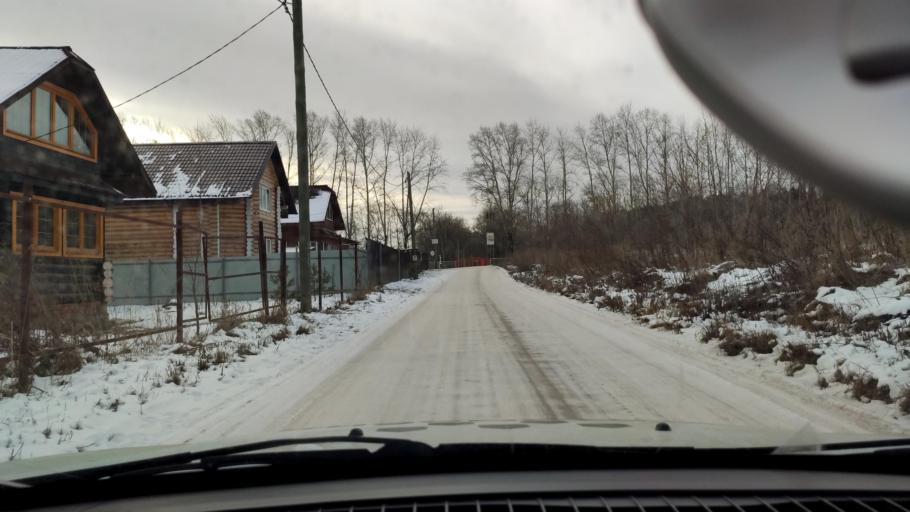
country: RU
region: Perm
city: Lobanovo
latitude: 57.8271
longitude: 56.3543
